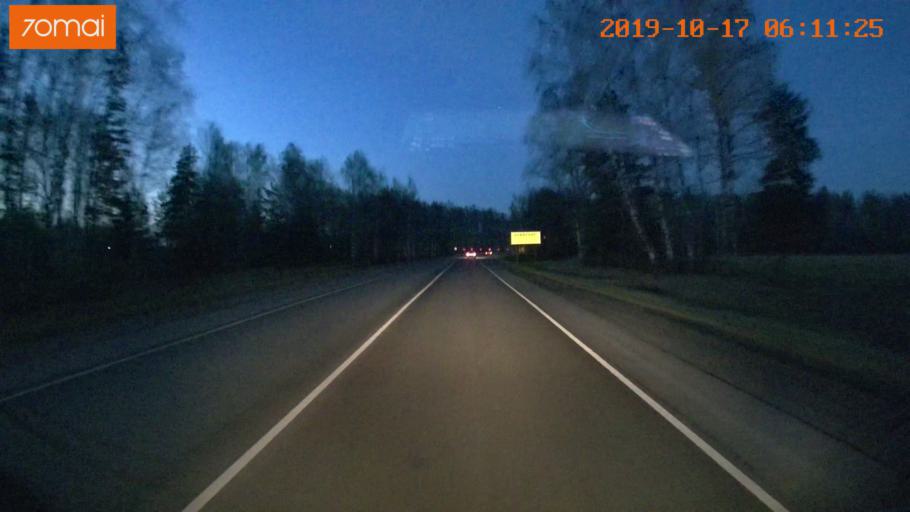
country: RU
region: Ivanovo
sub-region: Gorod Ivanovo
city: Ivanovo
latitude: 56.9194
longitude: 40.9580
